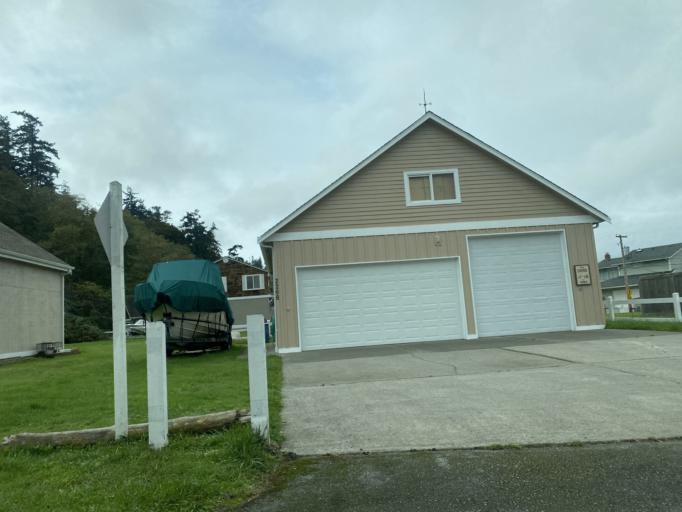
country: US
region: Washington
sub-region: Island County
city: Camano
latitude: 48.0958
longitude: -122.4919
